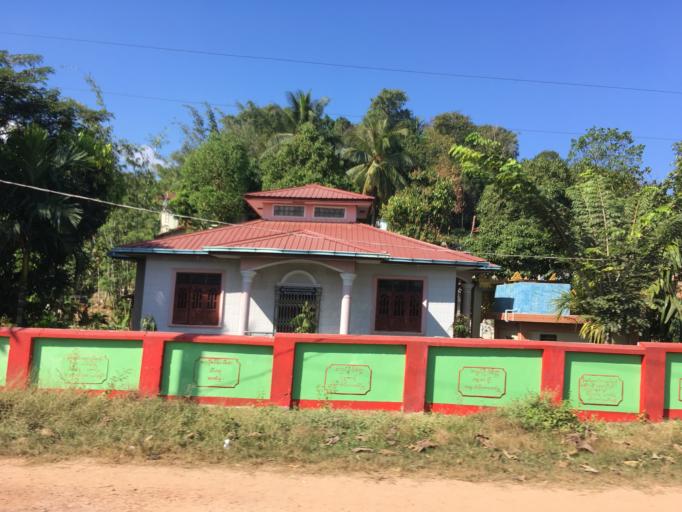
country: MM
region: Mon
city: Mawlamyine
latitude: 16.4749
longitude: 97.6332
